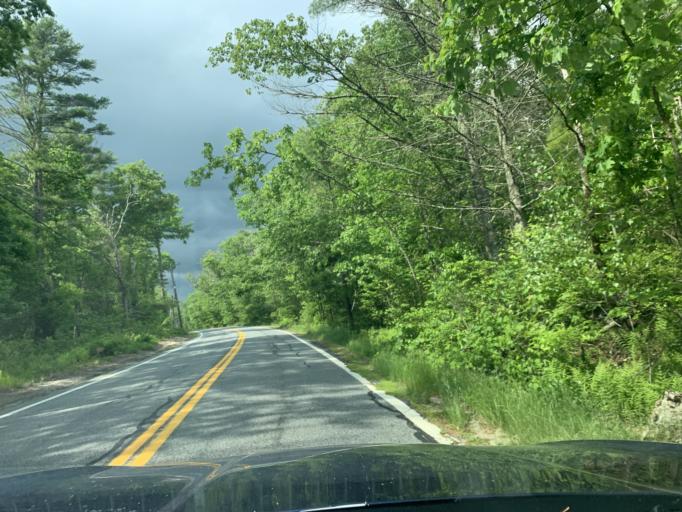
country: US
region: Rhode Island
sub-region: Kent County
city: Coventry
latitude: 41.7004
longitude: -71.7563
